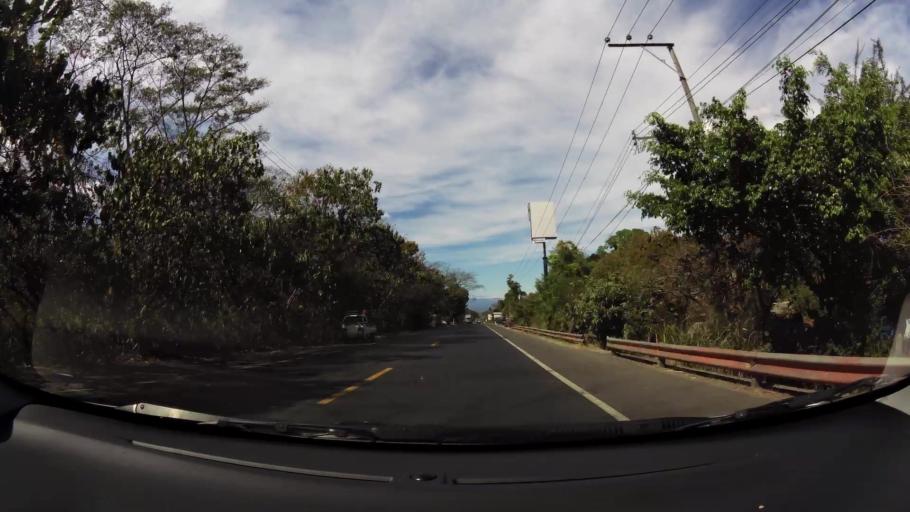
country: SV
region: San Salvador
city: Guazapa
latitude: 13.8811
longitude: -89.1744
